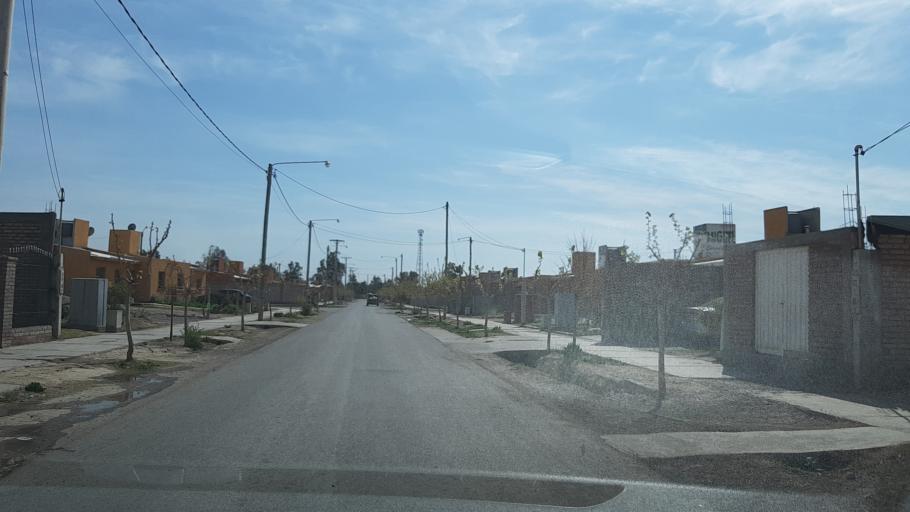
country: AR
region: San Juan
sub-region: Departamento de Zonda
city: Zonda
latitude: -31.5467
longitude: -68.7396
